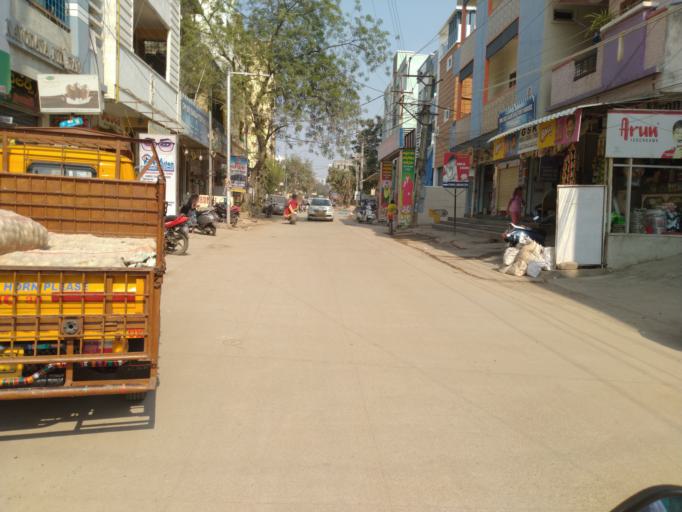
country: IN
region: Telangana
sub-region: Rangareddi
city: Quthbullapur
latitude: 17.4958
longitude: 78.4653
